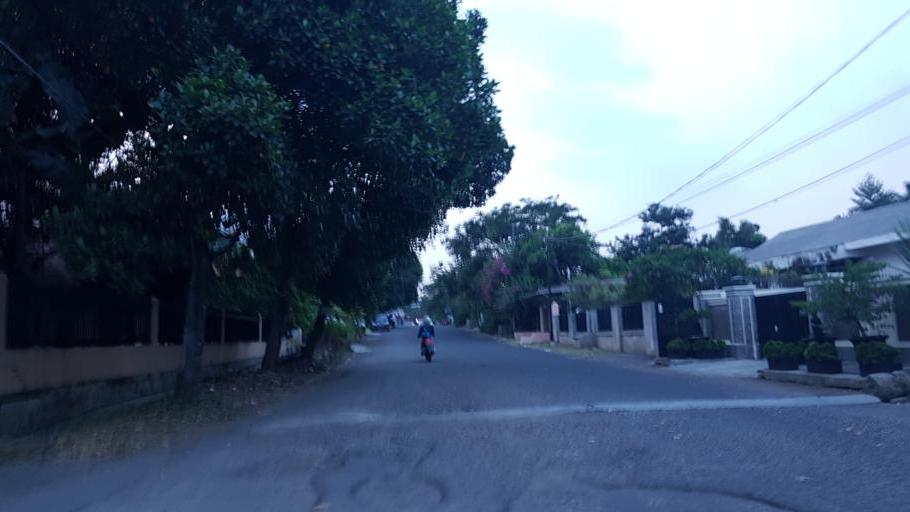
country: ID
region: West Java
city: Pamulang
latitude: -6.3192
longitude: 106.7860
